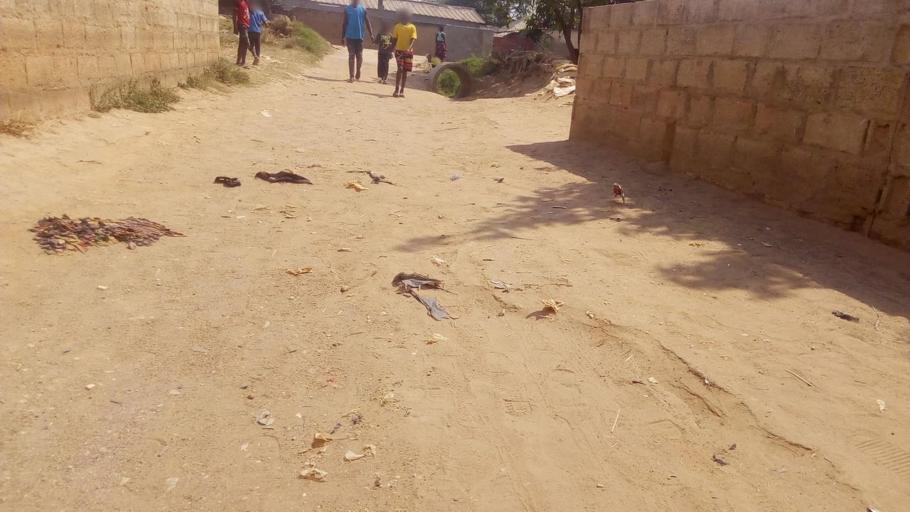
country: ZM
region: Lusaka
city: Lusaka
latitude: -15.3569
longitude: 28.2976
